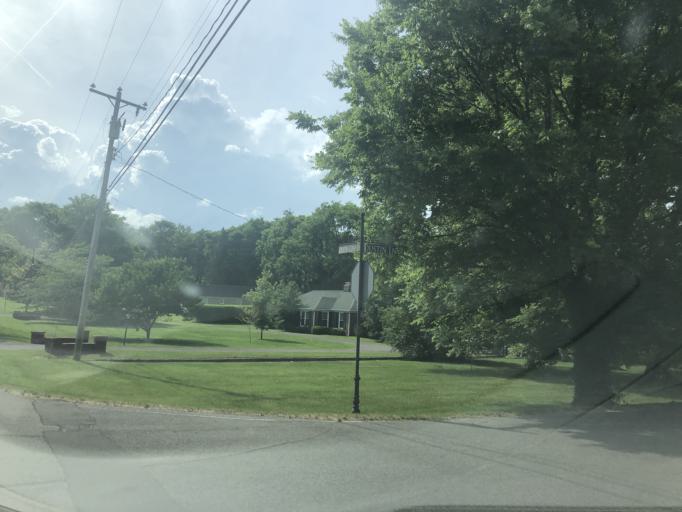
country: US
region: Tennessee
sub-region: Davidson County
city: Oak Hill
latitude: 36.0833
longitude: -86.7848
